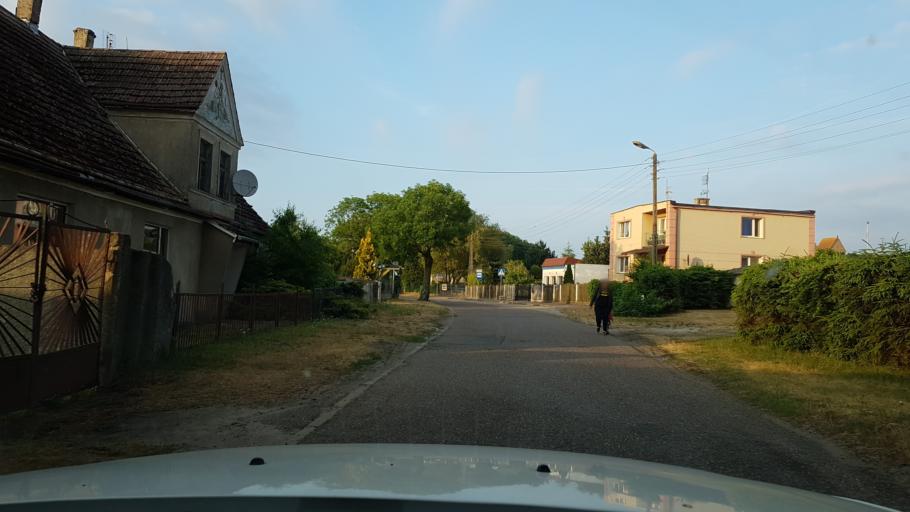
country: PL
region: West Pomeranian Voivodeship
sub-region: Swinoujscie
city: Swinoujscie
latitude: 53.8532
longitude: 14.3013
